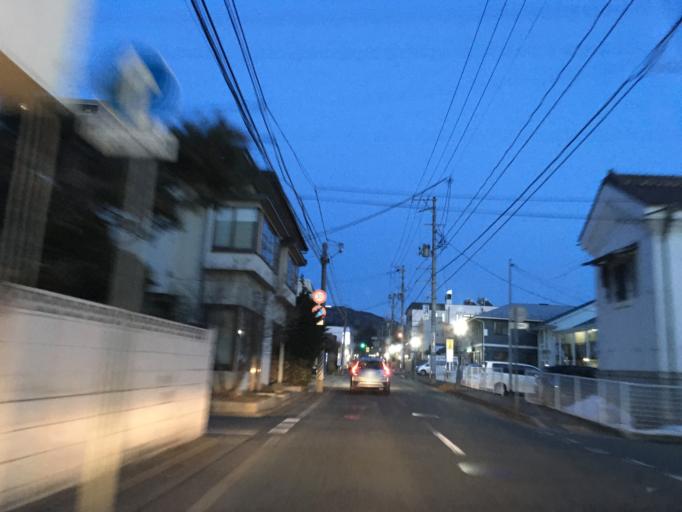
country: JP
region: Iwate
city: Morioka-shi
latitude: 39.7045
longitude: 141.1589
